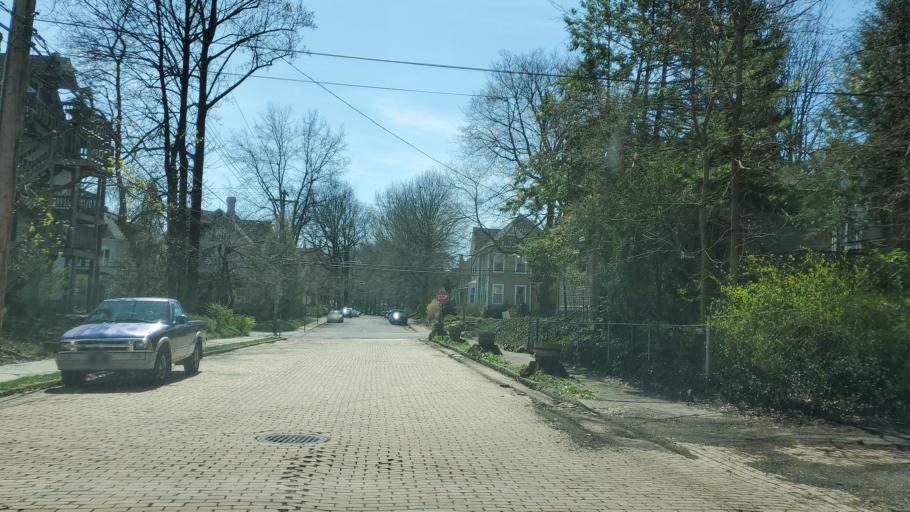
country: US
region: Pennsylvania
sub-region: Allegheny County
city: Wilkinsburg
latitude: 40.4382
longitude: -79.8934
